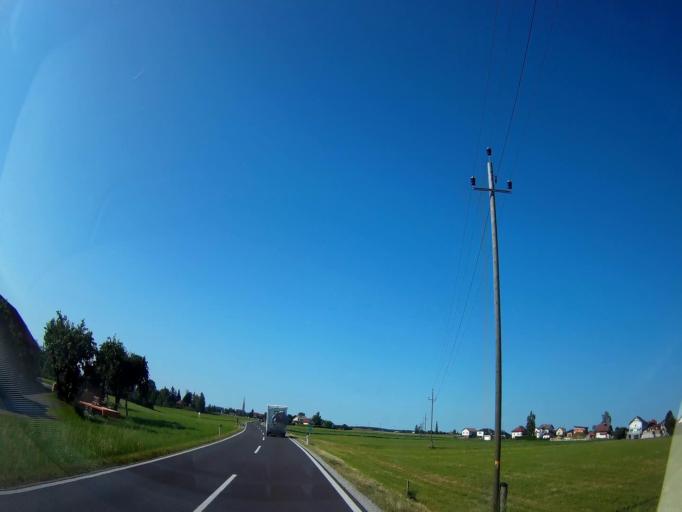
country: AT
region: Upper Austria
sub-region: Politischer Bezirk Braunau am Inn
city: Braunau am Inn
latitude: 48.1652
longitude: 13.0499
